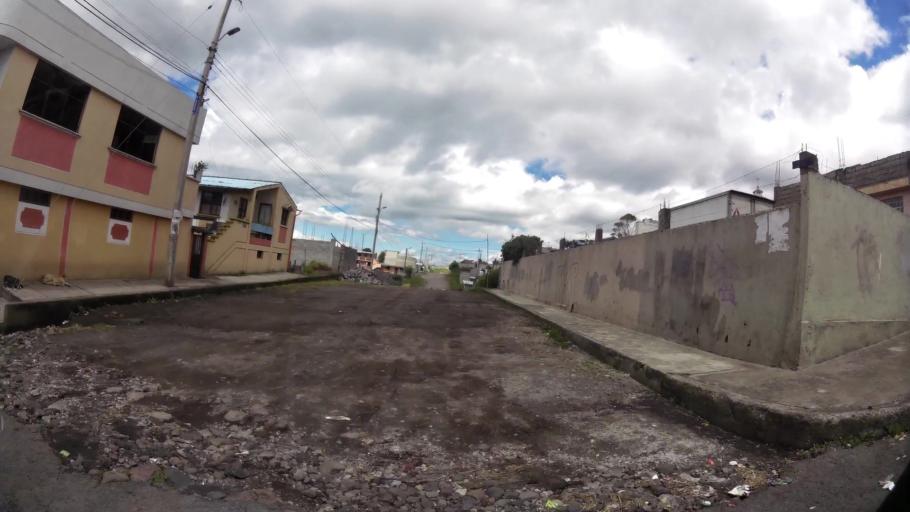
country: EC
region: Pichincha
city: Sangolqui
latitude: -0.3420
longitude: -78.5682
